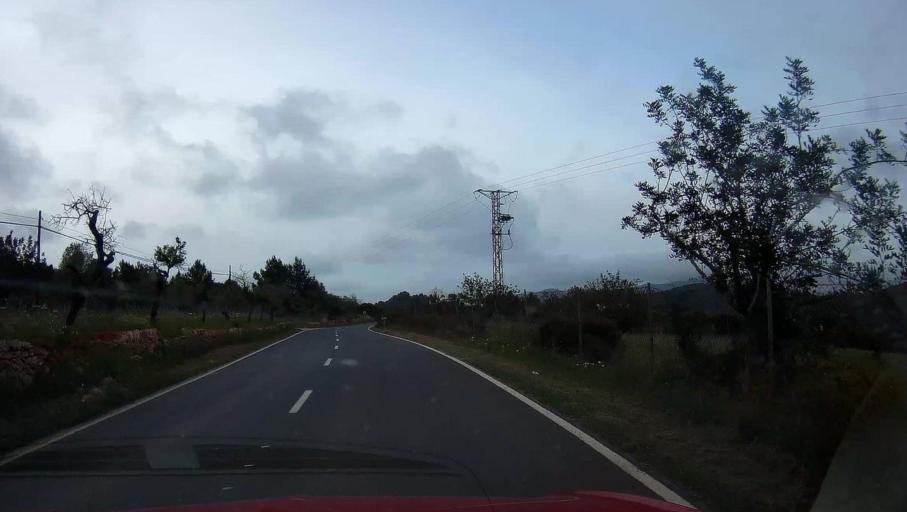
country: ES
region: Balearic Islands
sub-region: Illes Balears
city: Sant Joan de Labritja
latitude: 39.0509
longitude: 1.4333
